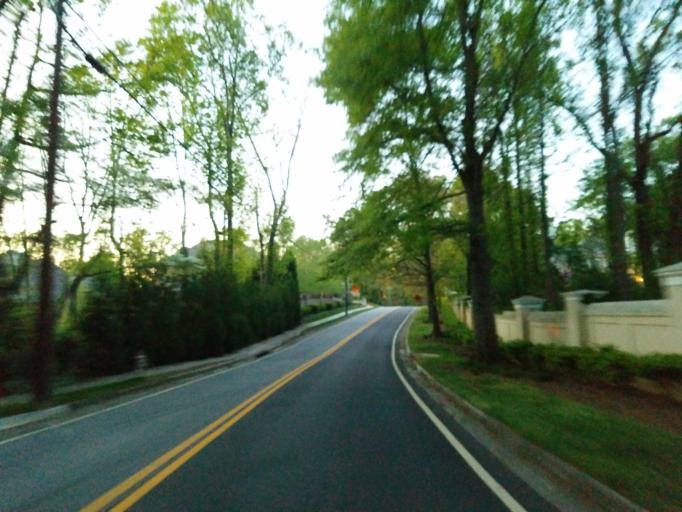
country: US
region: Georgia
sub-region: Fulton County
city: Sandy Springs
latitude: 33.9073
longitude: -84.4184
